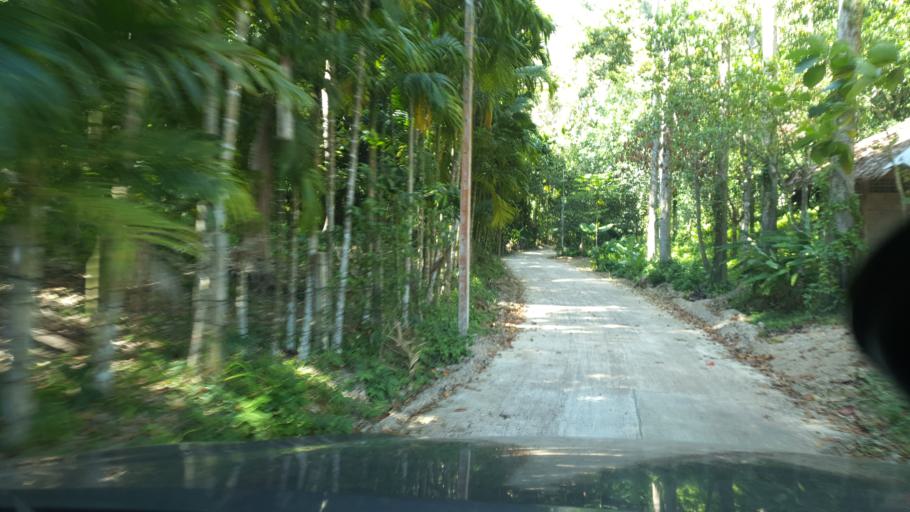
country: TH
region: Phangnga
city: Ban Ao Nang
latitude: 8.0250
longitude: 98.8537
